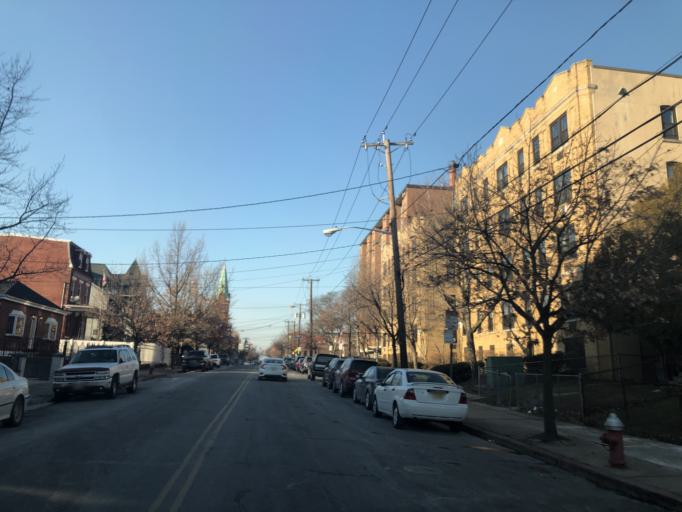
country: US
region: New Jersey
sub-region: Hudson County
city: Bayonne
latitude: 40.6941
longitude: -74.0894
